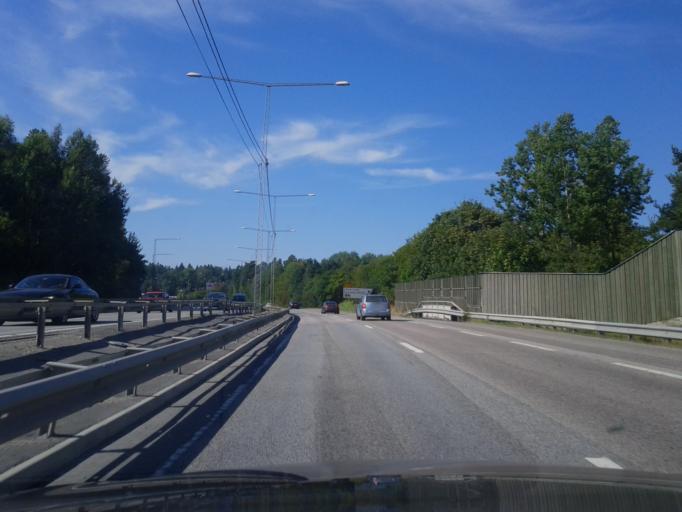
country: SE
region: Stockholm
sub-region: Taby Kommun
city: Taby
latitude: 59.4367
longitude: 18.0746
